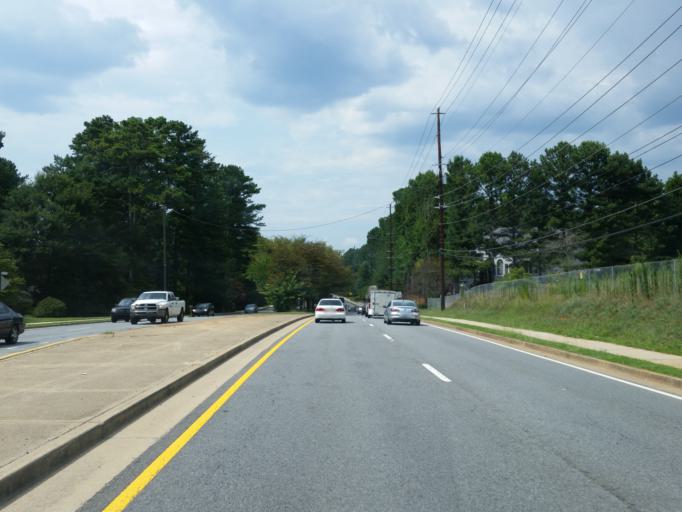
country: US
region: Georgia
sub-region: Cobb County
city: Vinings
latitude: 33.9325
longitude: -84.4609
